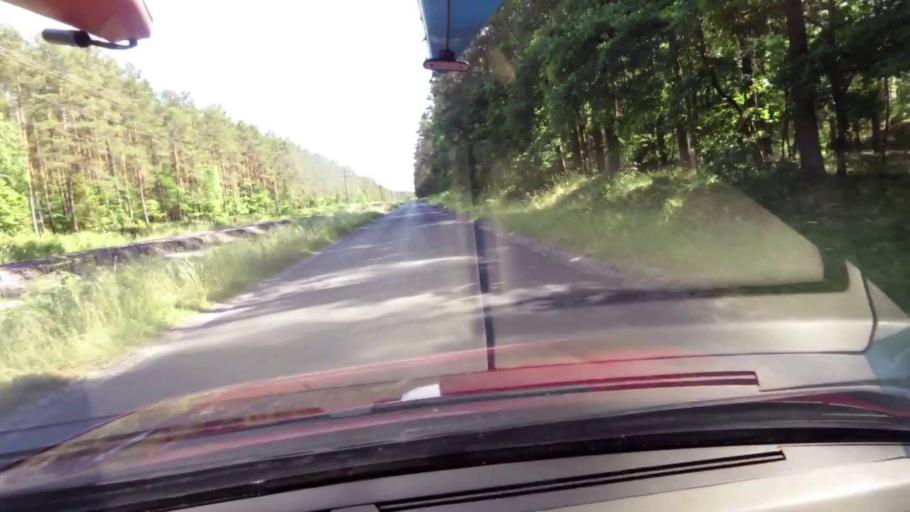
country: PL
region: Pomeranian Voivodeship
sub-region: Powiat slupski
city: Kepice
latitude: 54.2296
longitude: 16.8943
